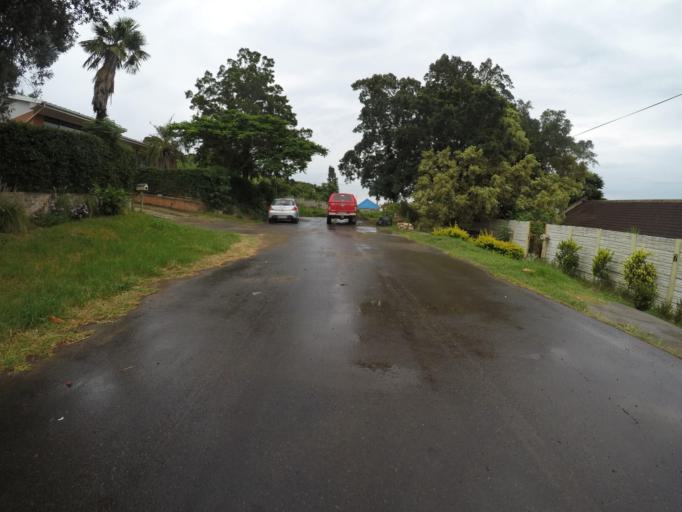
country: ZA
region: Eastern Cape
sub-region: Buffalo City Metropolitan Municipality
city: East London
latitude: -32.9647
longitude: 27.8459
